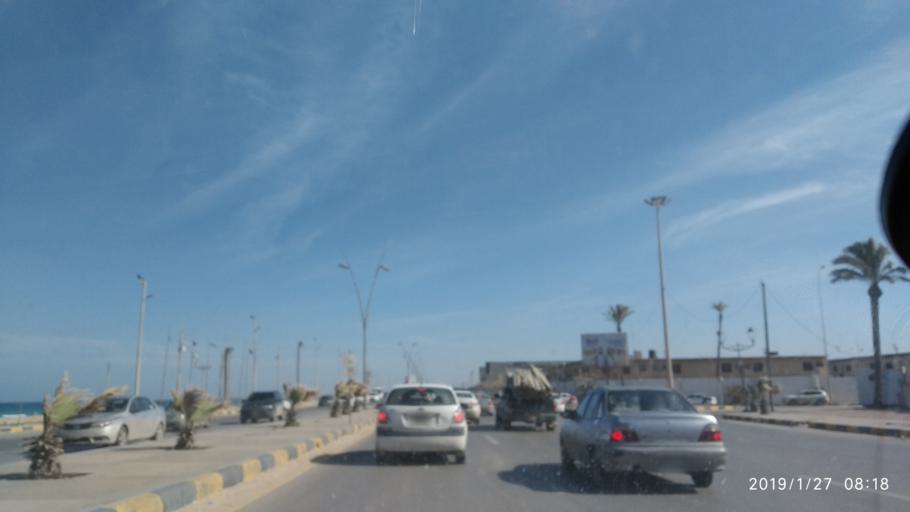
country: LY
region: Tripoli
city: Tagiura
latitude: 32.9077
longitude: 13.2709
